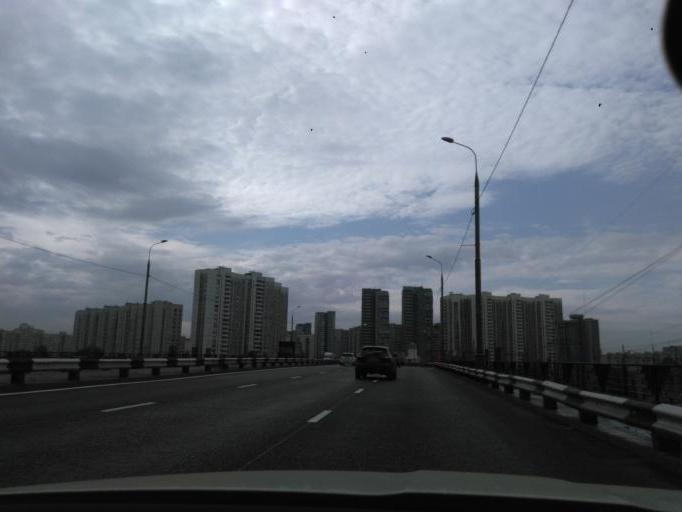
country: RU
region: Moscow
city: Novovladykino
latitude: 55.8342
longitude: 37.5781
